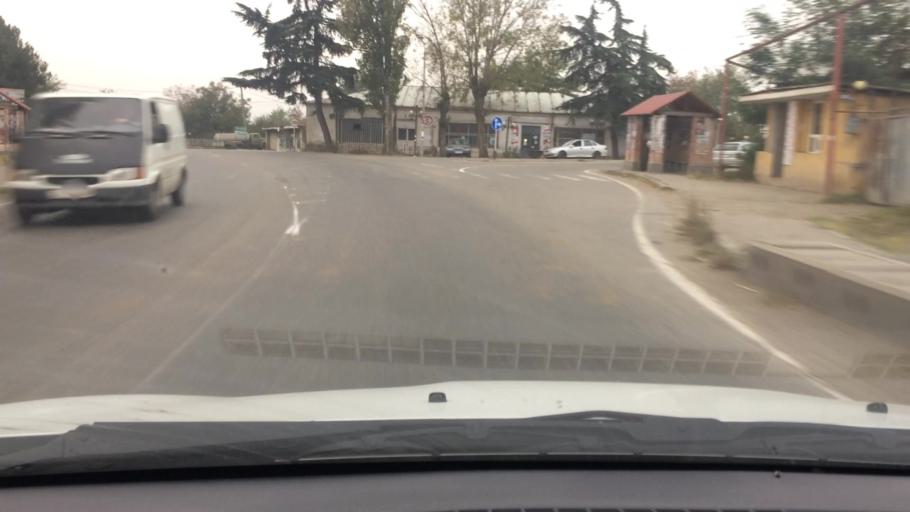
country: GE
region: Kvemo Kartli
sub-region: Marneuli
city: Marneuli
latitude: 41.5802
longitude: 44.7746
